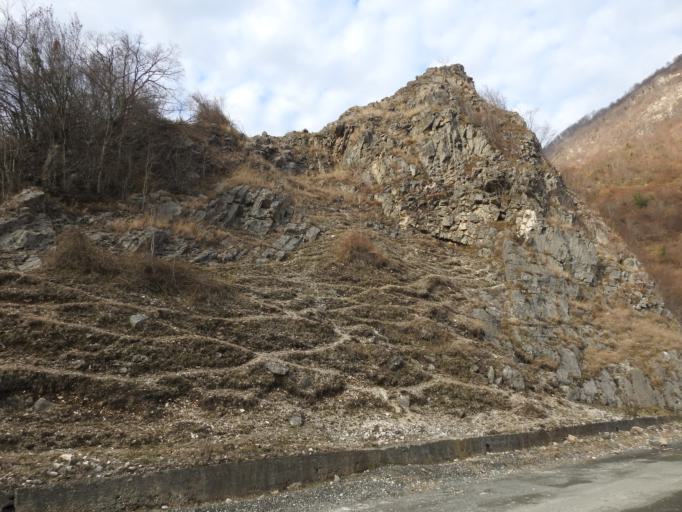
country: GE
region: Abkhazia
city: Tqvarch'eli
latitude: 42.8401
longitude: 41.6973
